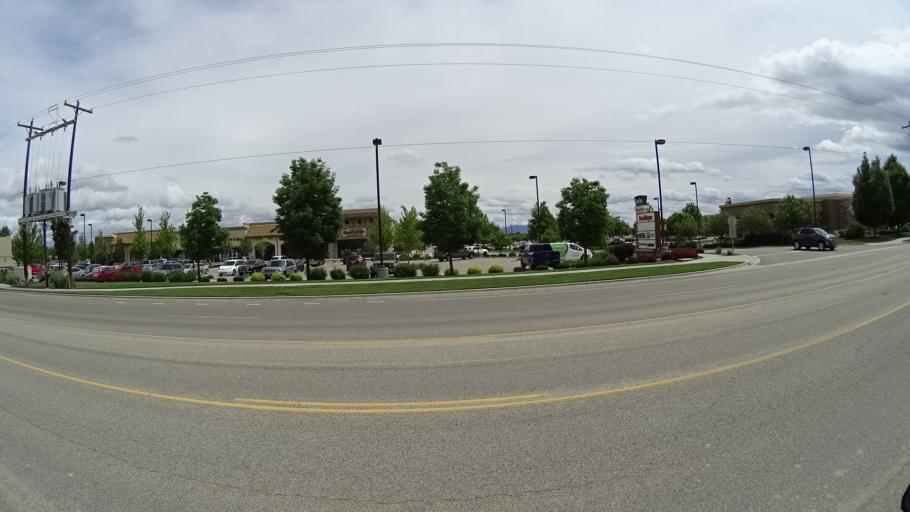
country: US
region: Idaho
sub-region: Ada County
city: Meridian
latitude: 43.6655
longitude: -116.4138
